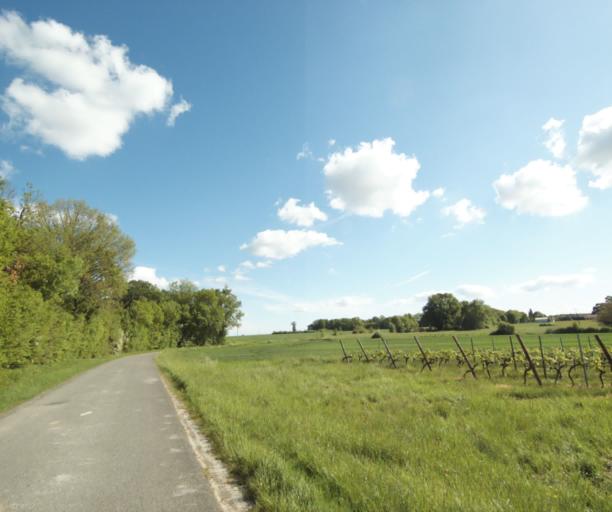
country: FR
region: Poitou-Charentes
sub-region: Departement de la Charente-Maritime
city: Chermignac
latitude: 45.7271
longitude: -0.6892
